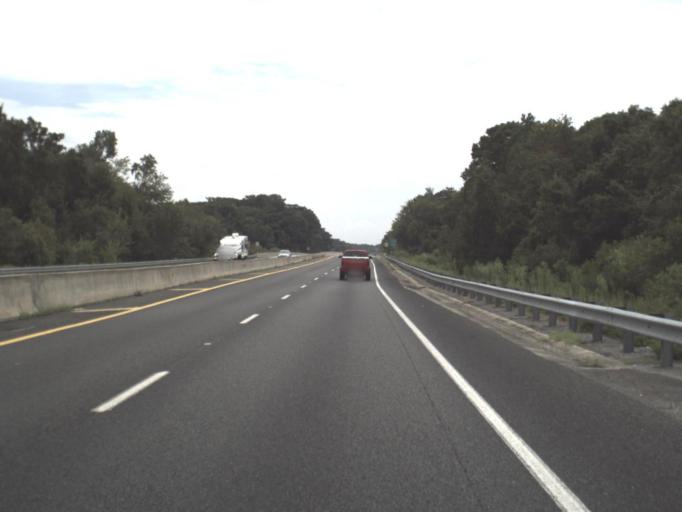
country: US
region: Florida
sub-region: Citrus County
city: Inverness
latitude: 28.8513
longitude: -82.2242
